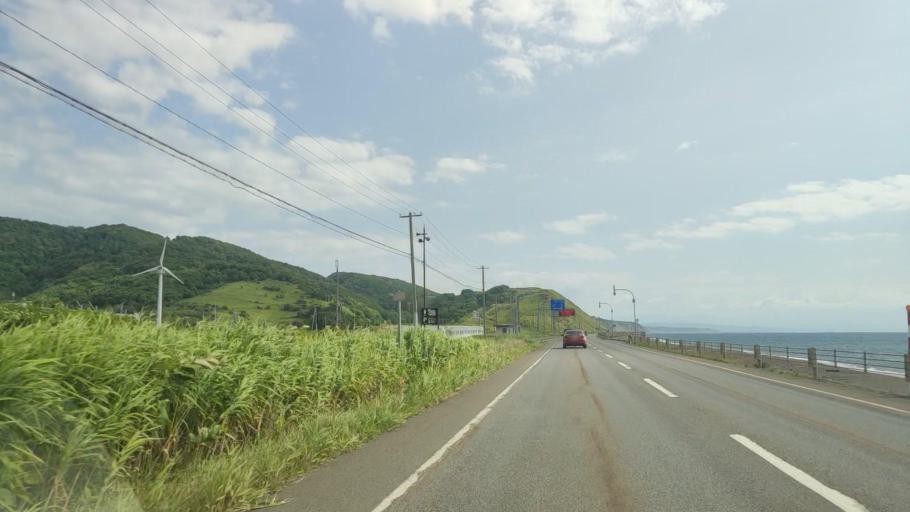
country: JP
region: Hokkaido
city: Rumoi
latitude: 44.0751
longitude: 141.6628
